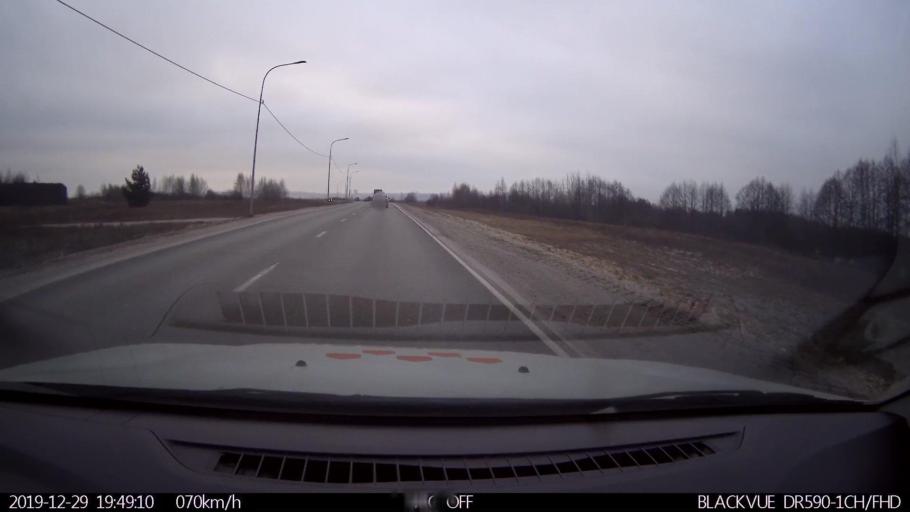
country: RU
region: Nizjnij Novgorod
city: Nizhniy Novgorod
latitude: 56.3771
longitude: 44.0134
